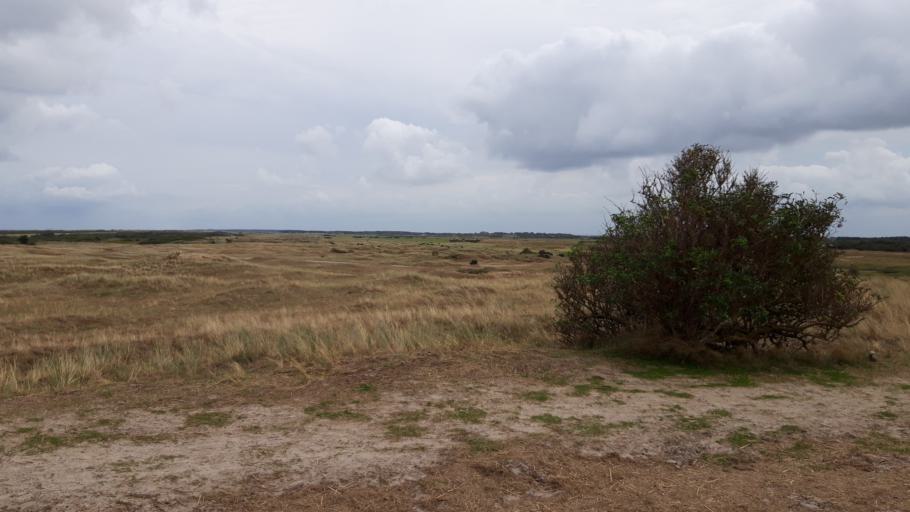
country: NL
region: Friesland
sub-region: Gemeente Ameland
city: Hollum
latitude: 53.4559
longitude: 5.6410
